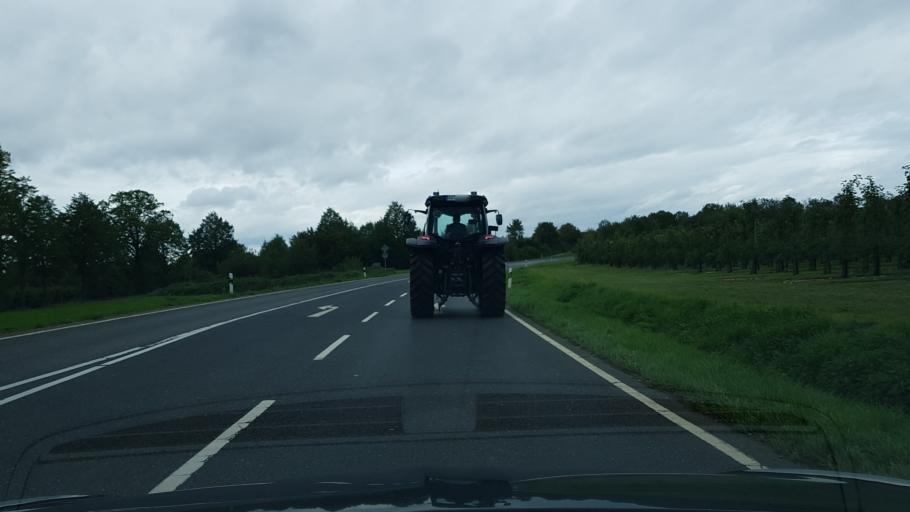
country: DE
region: North Rhine-Westphalia
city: Meckenheim
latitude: 50.6162
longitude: 7.0399
